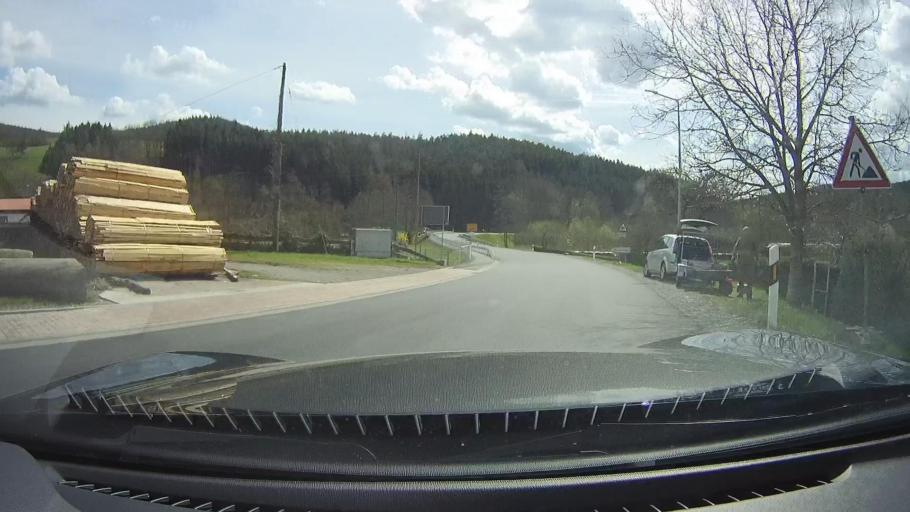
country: DE
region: Bavaria
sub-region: Regierungsbezirk Unterfranken
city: Kirchzell
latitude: 49.6136
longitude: 9.1680
